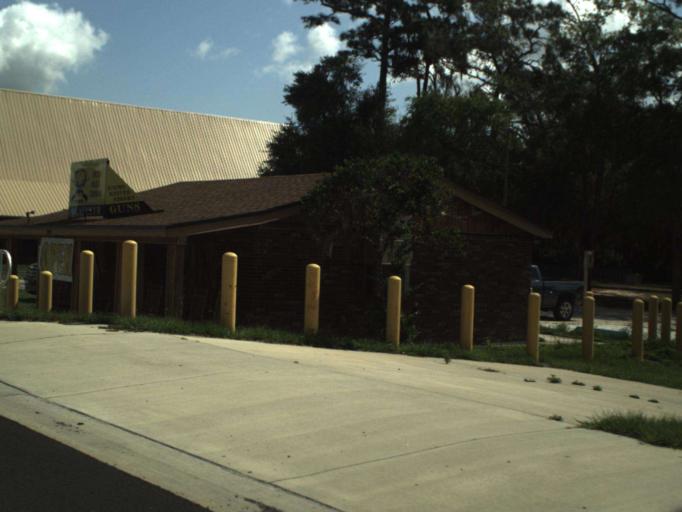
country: US
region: Florida
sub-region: Seminole County
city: Midway
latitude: 28.8496
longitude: -81.1620
